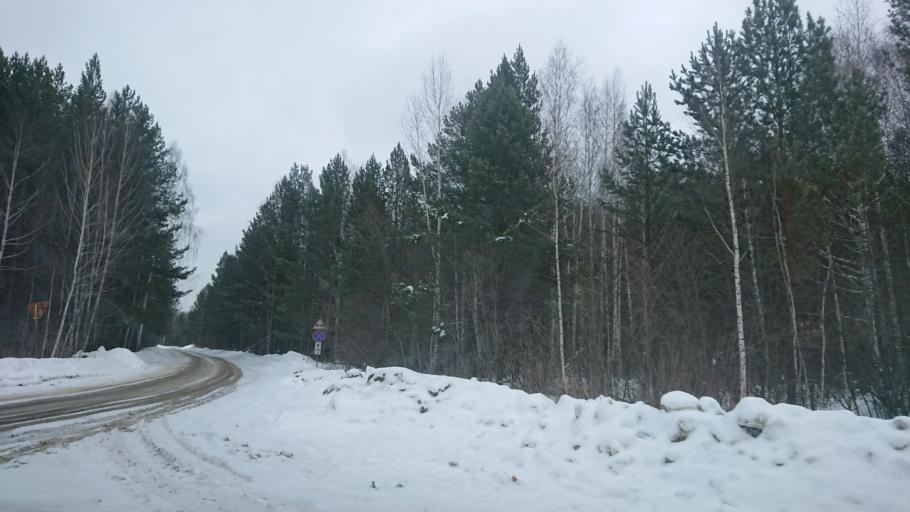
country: RU
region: Sverdlovsk
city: Sysert'
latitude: 56.4443
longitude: 60.8834
